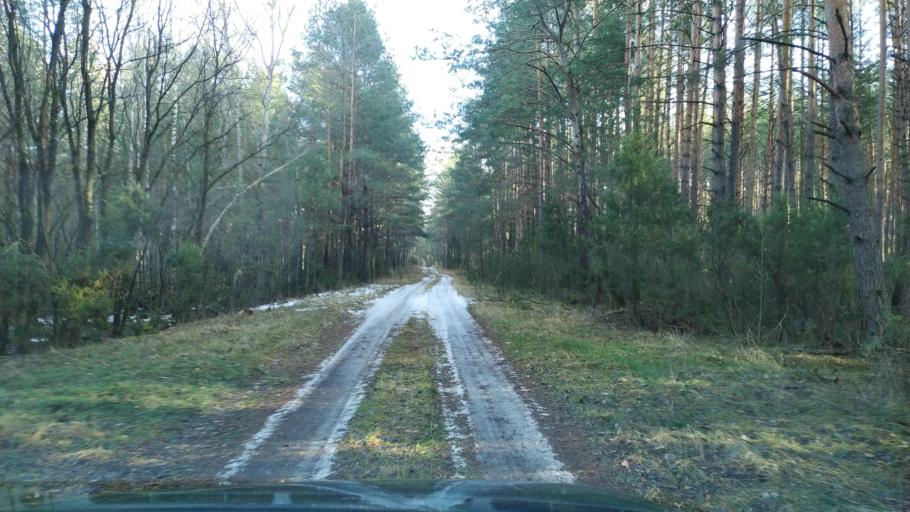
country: BY
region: Brest
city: Kamyanyets
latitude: 52.4304
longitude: 24.0027
